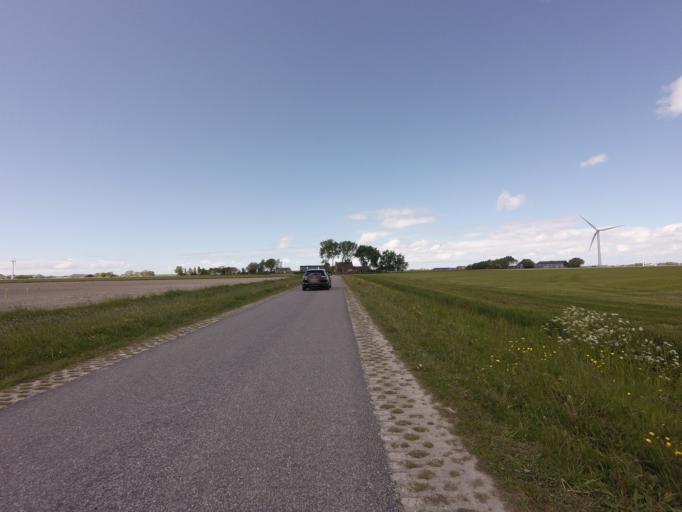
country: NL
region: Friesland
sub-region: Gemeente Harlingen
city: Harlingen
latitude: 53.1187
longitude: 5.4346
